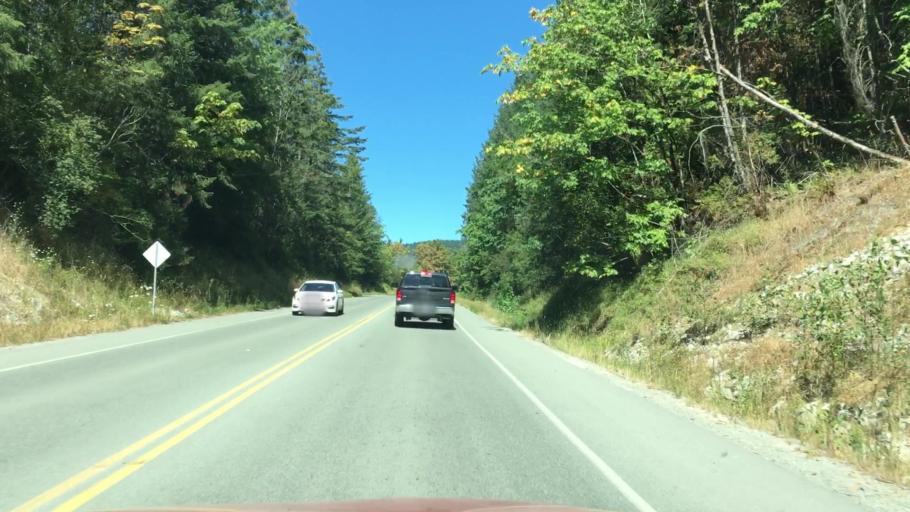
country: CA
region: British Columbia
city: Port Alberni
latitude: 49.2610
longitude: -124.7687
